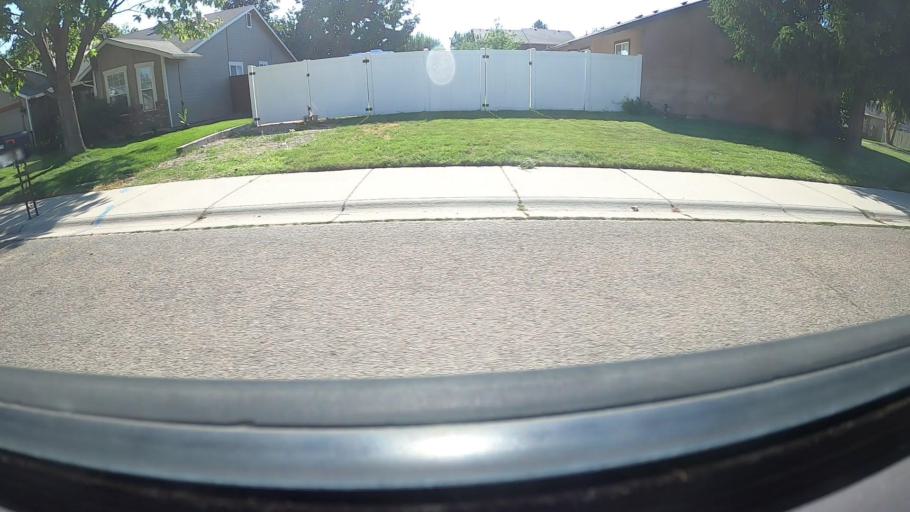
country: US
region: Idaho
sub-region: Ada County
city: Meridian
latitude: 43.6260
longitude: -116.3659
